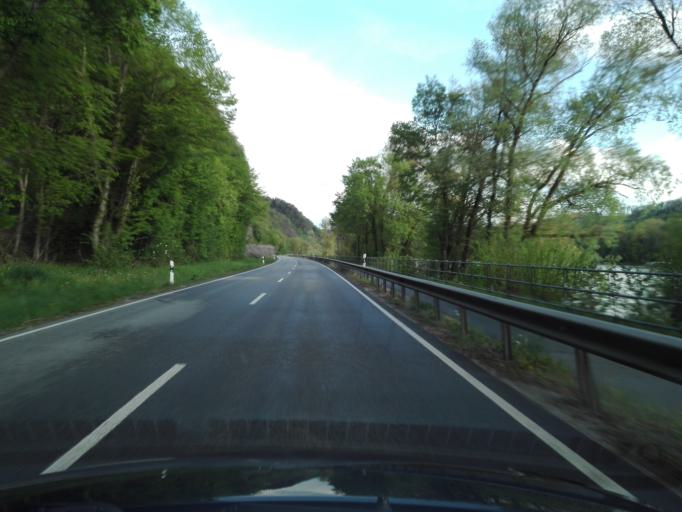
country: DE
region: Bavaria
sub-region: Lower Bavaria
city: Thyrnau
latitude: 48.5832
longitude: 13.5352
